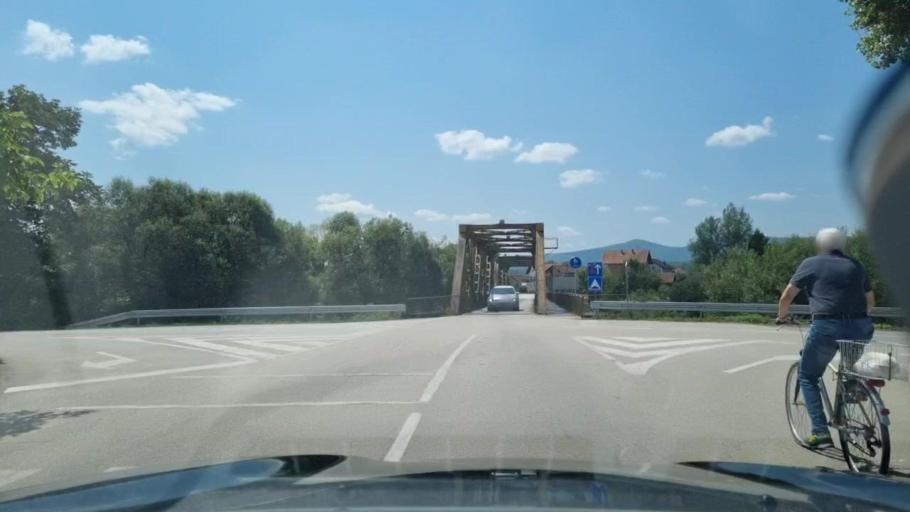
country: BA
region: Federation of Bosnia and Herzegovina
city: Sanski Most
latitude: 44.7573
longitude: 16.6753
